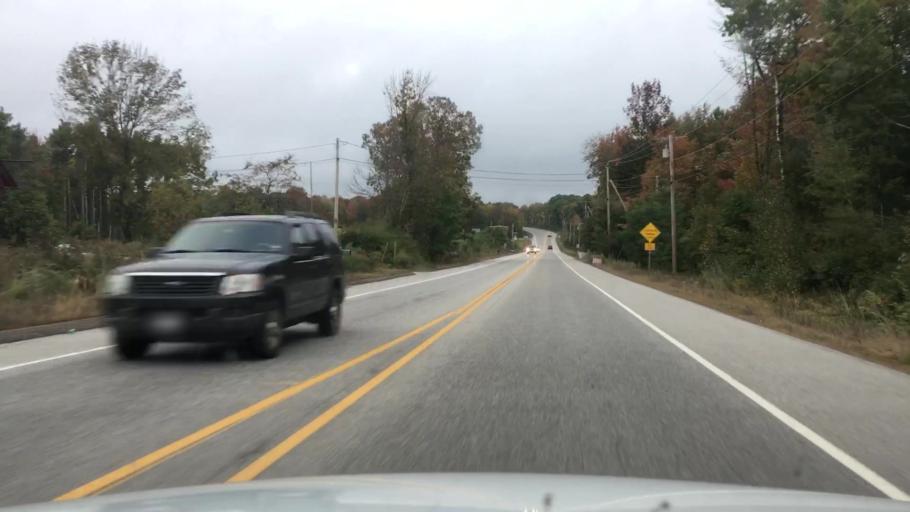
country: US
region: Maine
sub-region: Androscoggin County
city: Poland
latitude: 44.0158
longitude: -70.3631
